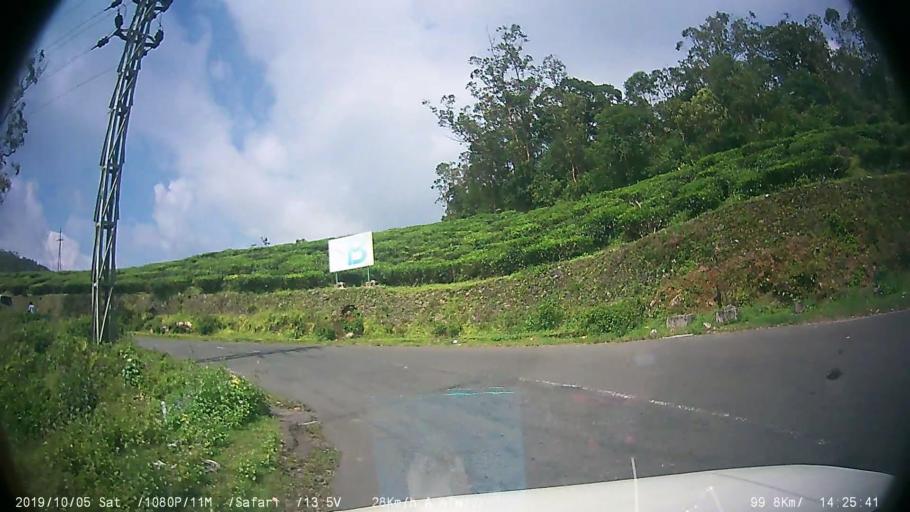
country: IN
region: Kerala
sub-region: Kottayam
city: Erattupetta
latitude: 9.5967
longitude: 76.9694
